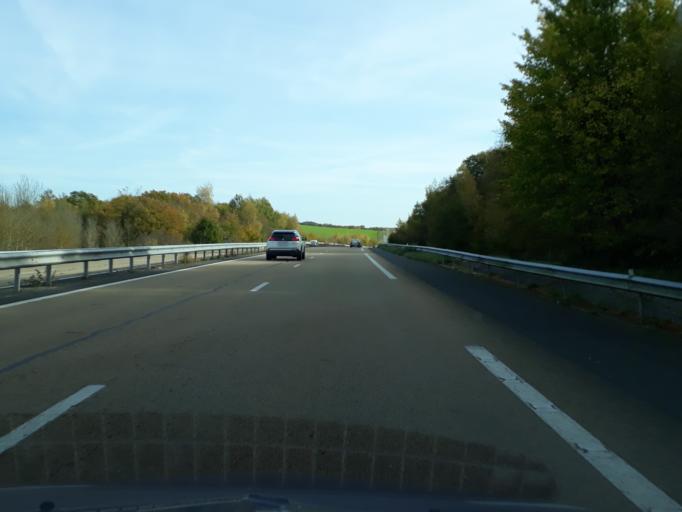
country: FR
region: Champagne-Ardenne
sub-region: Departement de l'Aube
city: Aix-en-Othe
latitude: 48.2577
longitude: 3.6494
